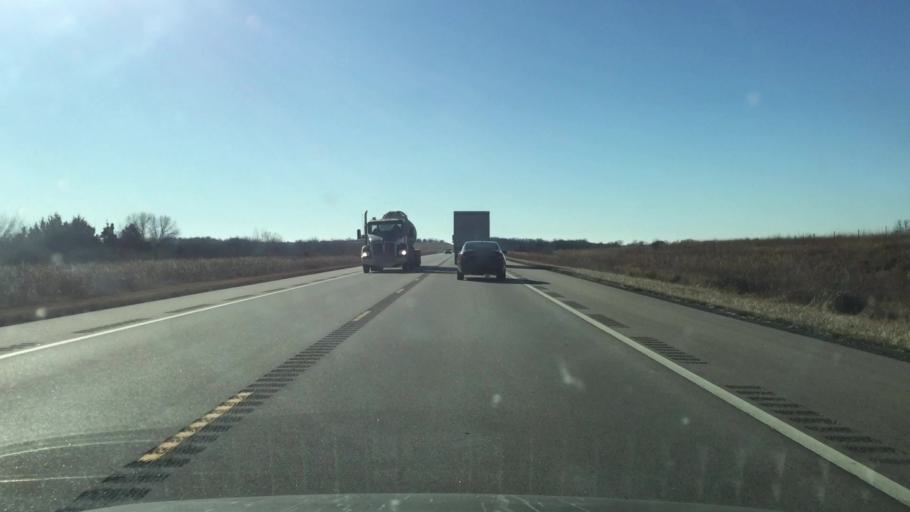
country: US
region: Kansas
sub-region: Allen County
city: Iola
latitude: 38.0305
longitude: -95.3788
